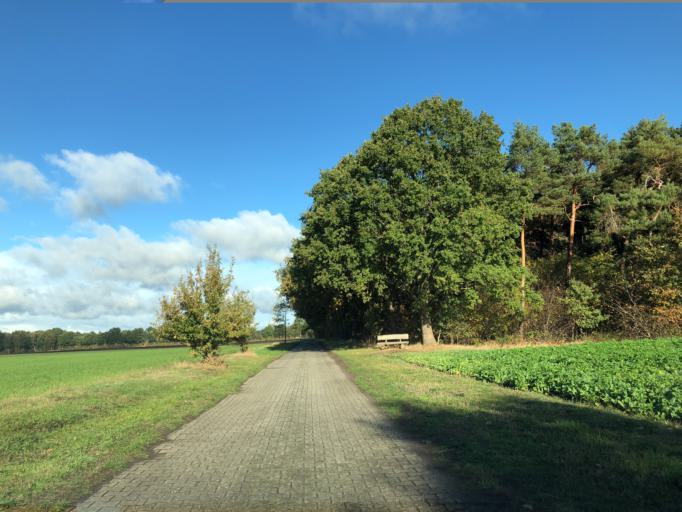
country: DE
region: Lower Saxony
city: Neulehe
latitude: 53.0223
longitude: 7.3677
